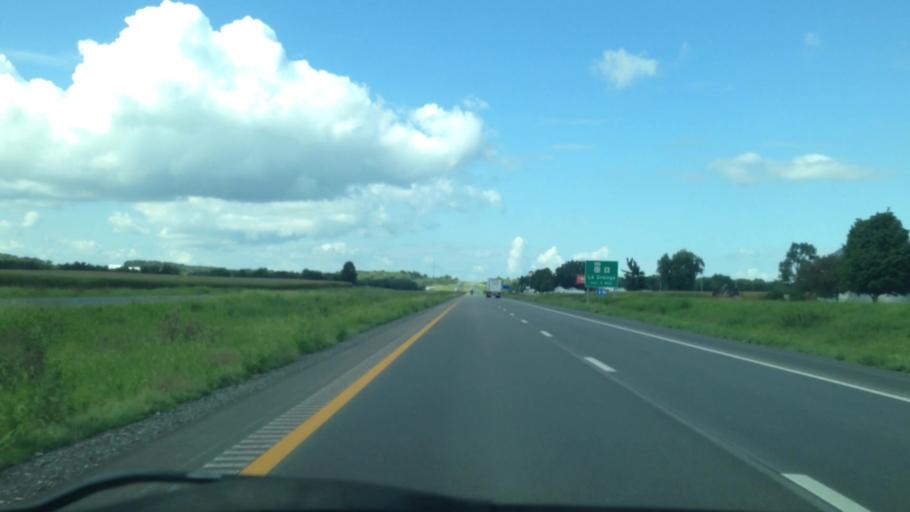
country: US
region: Illinois
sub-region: Adams County
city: Quincy
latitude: 39.9926
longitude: -91.5267
